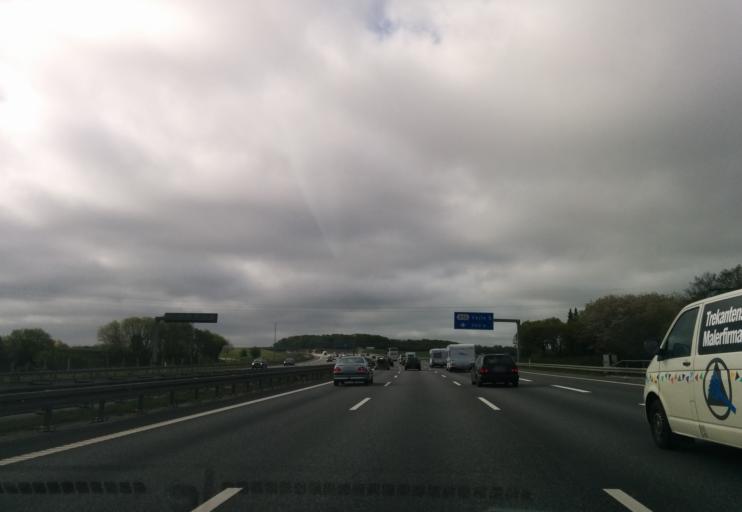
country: DK
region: South Denmark
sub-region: Vejle Kommune
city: Vejle
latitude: 55.6723
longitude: 9.5535
